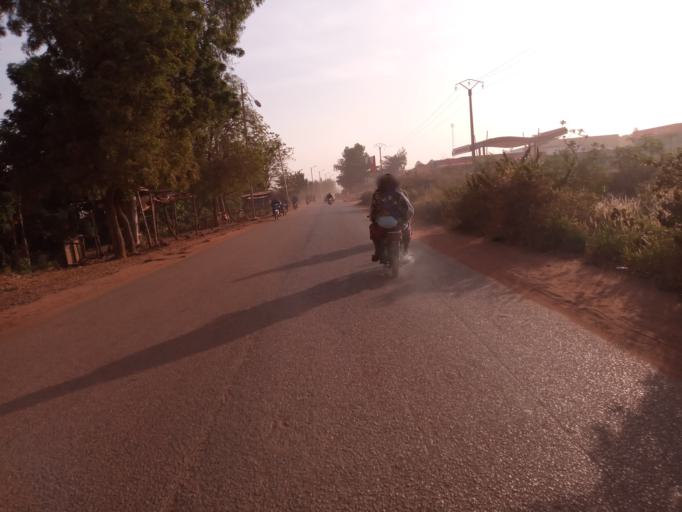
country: ML
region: Bamako
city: Bamako
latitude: 12.6341
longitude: -7.9369
